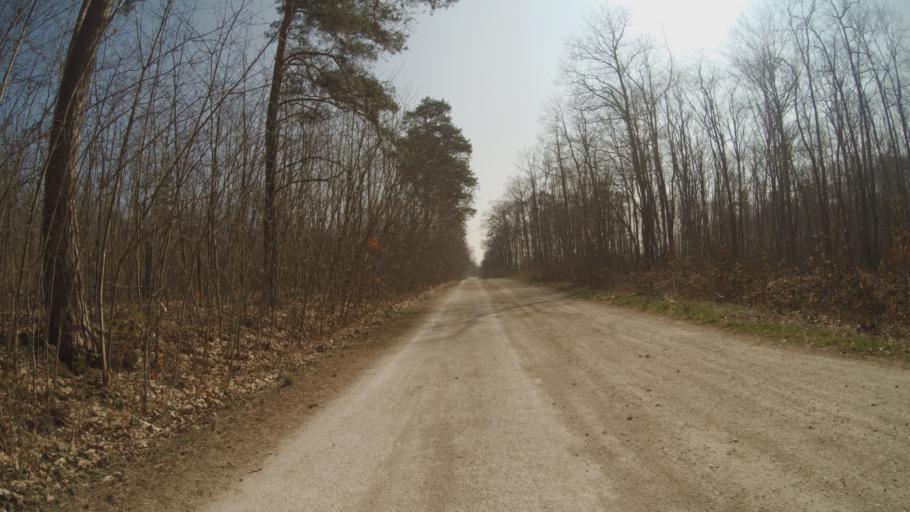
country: FR
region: Centre
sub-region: Departement du Loiret
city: Saint-Jean-de-Braye
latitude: 47.9367
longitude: 1.9815
